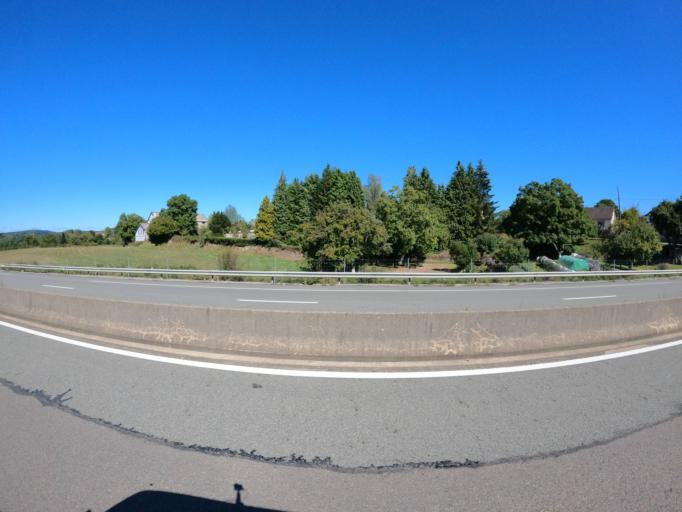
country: FR
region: Limousin
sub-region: Departement de la Creuse
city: Saint-Vaury
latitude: 46.2006
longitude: 1.7525
